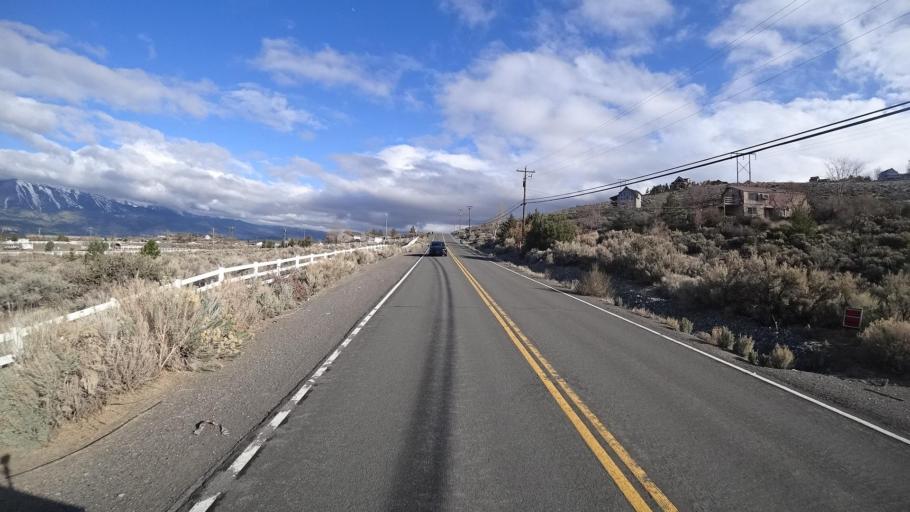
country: US
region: Nevada
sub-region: Storey County
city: Virginia City
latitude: 39.2798
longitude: -119.7575
